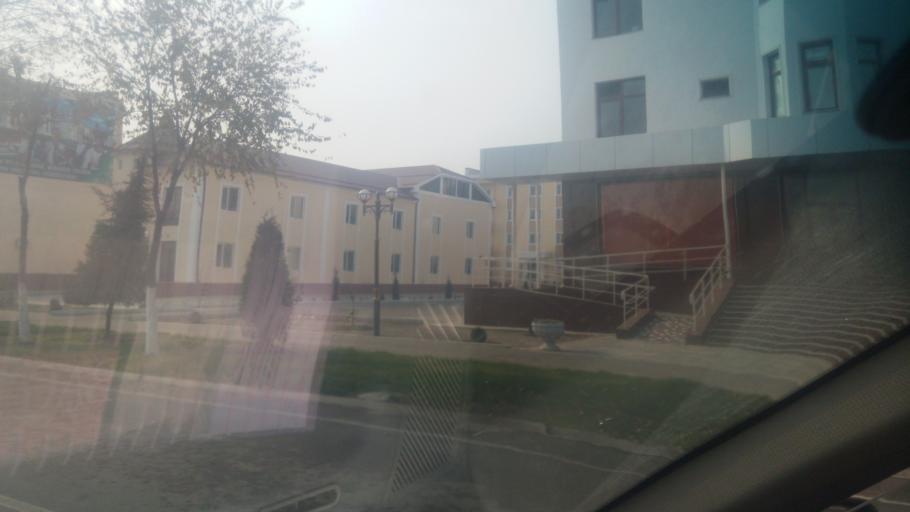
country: UZ
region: Sirdaryo
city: Guliston
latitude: 40.5069
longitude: 68.7719
